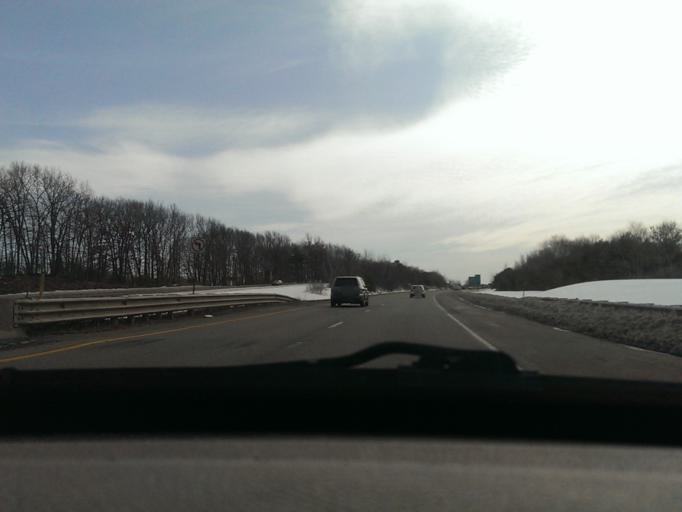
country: US
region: Massachusetts
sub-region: Worcester County
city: Whitinsville
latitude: 42.1150
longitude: -71.7057
